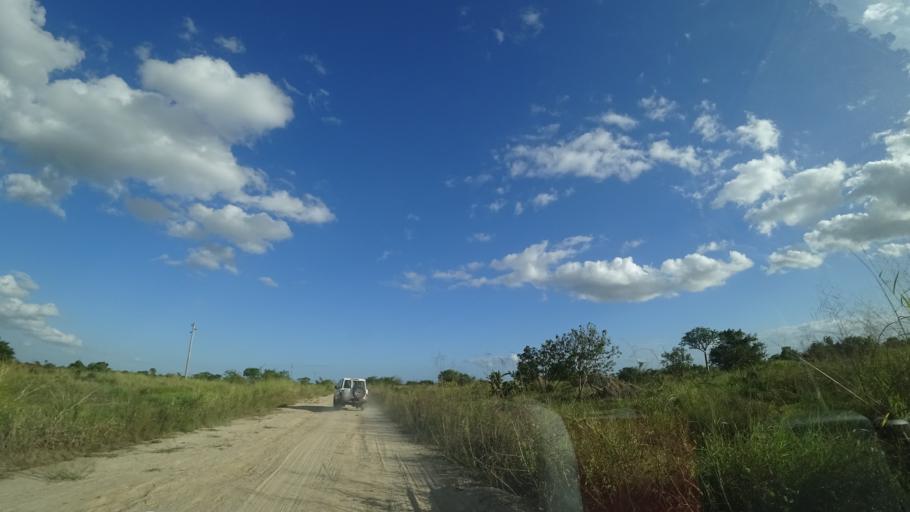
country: MZ
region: Sofala
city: Dondo
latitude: -19.4304
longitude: 34.5608
